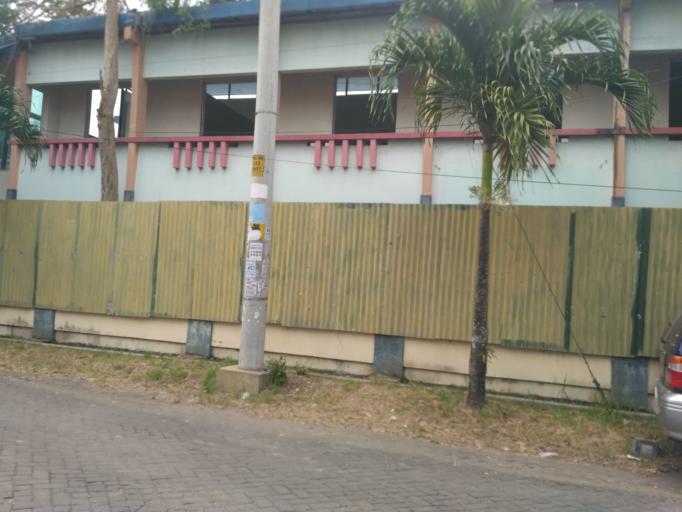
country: ID
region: Central Java
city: Semarang
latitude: -7.0562
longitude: 110.4319
